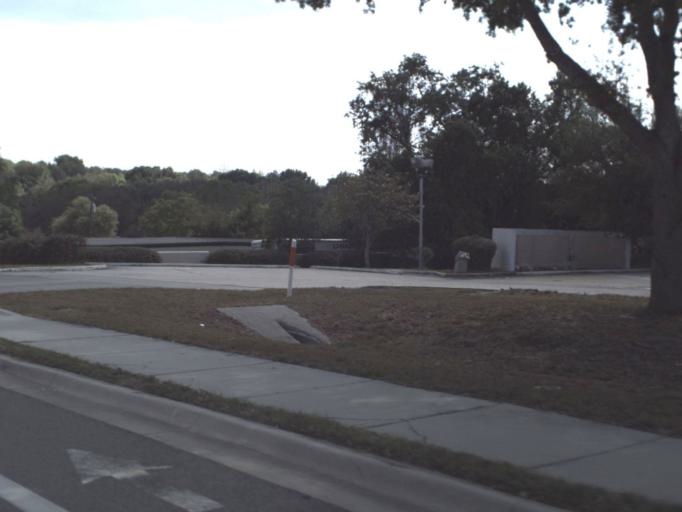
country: US
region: Florida
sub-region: Lake County
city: Clermont
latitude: 28.5429
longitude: -81.7418
